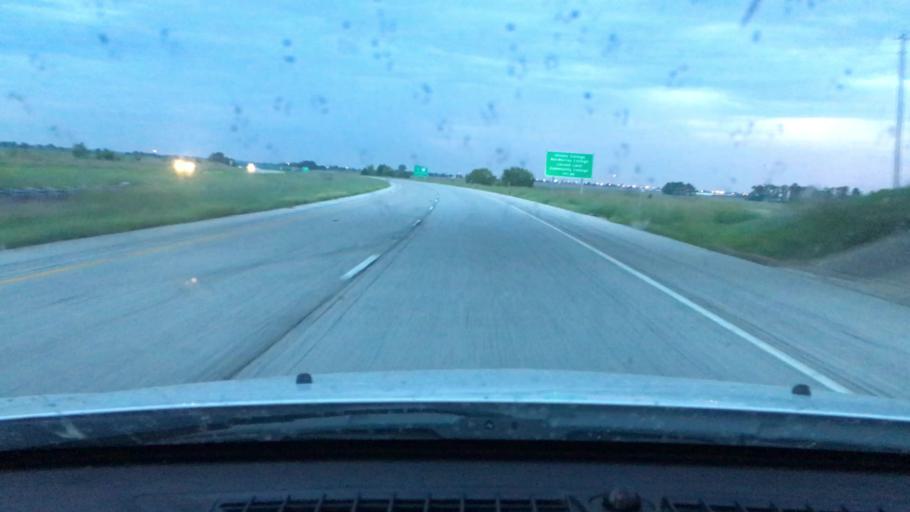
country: US
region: Illinois
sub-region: Morgan County
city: Jacksonville
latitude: 39.7351
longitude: -90.1555
